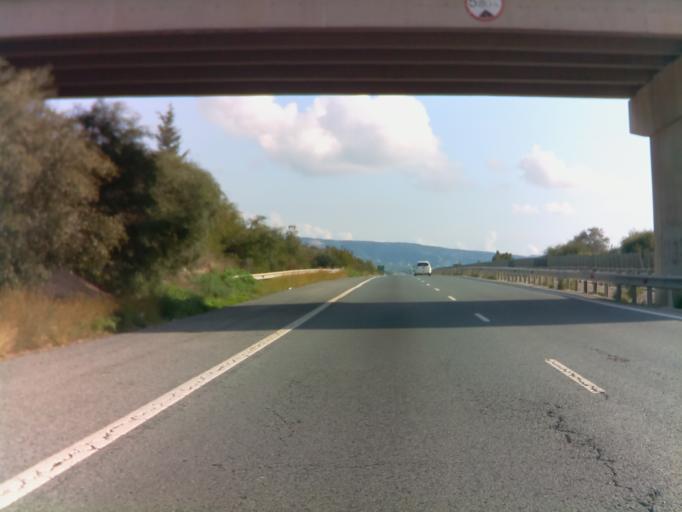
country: CY
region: Limassol
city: Pyrgos
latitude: 34.7460
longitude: 33.2931
